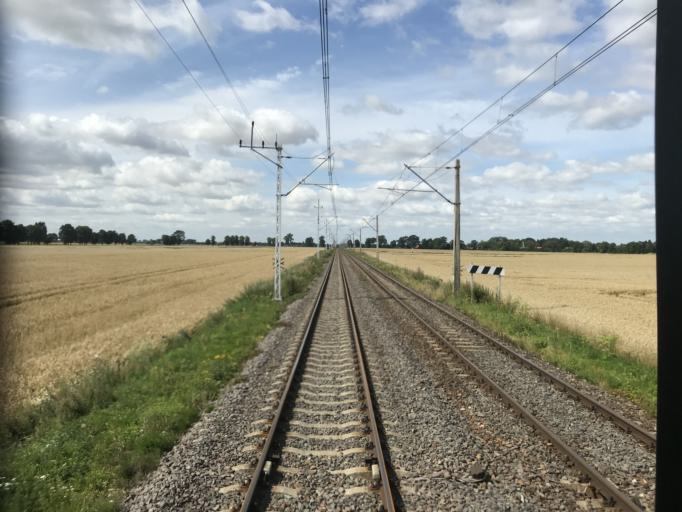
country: PL
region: Warmian-Masurian Voivodeship
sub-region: Powiat elblaski
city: Gronowo Elblaskie
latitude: 54.0721
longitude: 19.2604
